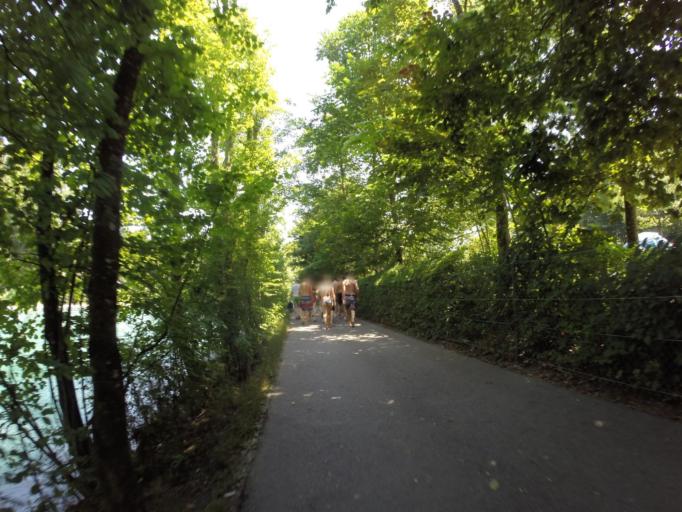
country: CH
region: Bern
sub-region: Bern-Mittelland District
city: Bern
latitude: 46.9329
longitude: 7.4532
